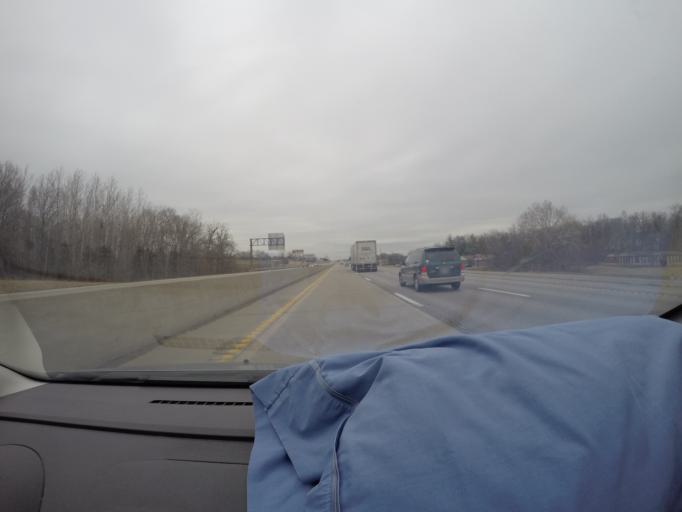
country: US
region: Missouri
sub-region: Saint Charles County
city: Lake Saint Louis
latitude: 38.8049
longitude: -90.7962
